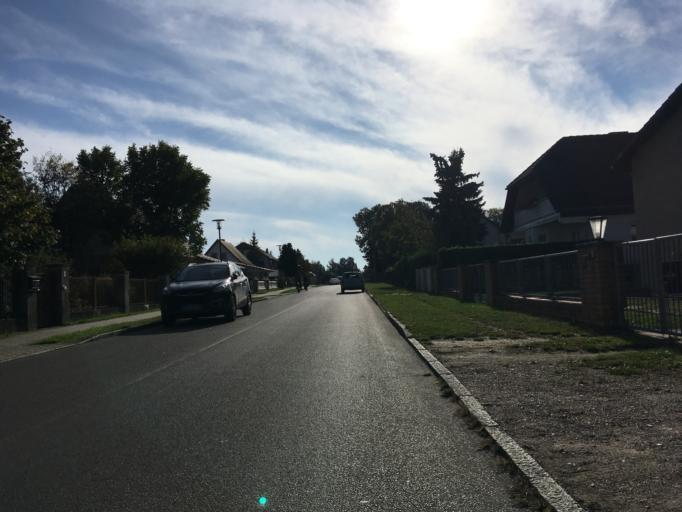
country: DE
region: Brandenburg
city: Hoppegarten
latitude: 52.5194
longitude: 13.6533
